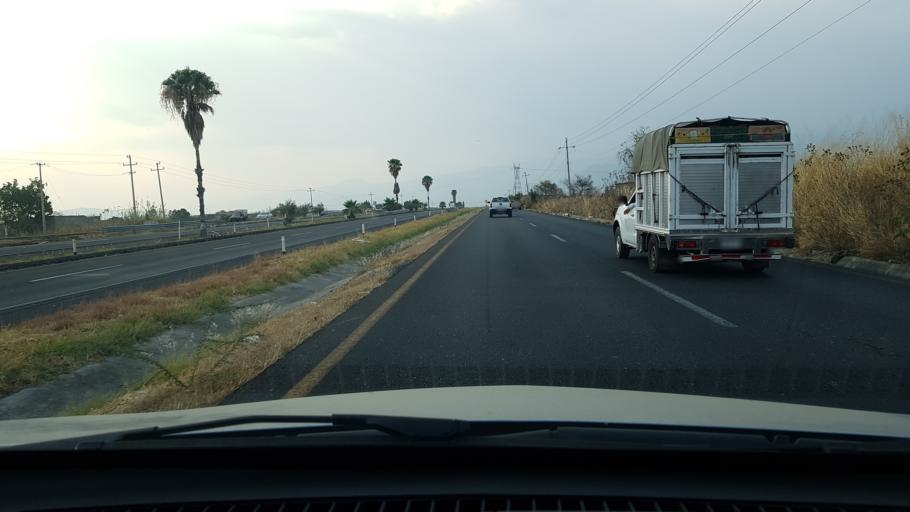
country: MX
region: Morelos
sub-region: Cuautla
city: Narciso Mendoza
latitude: 18.8733
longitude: -98.9571
